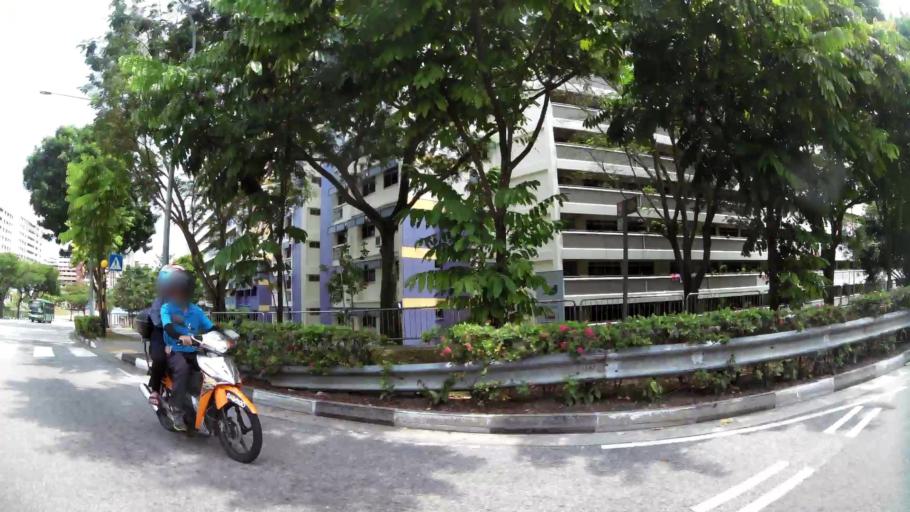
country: MY
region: Johor
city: Johor Bahru
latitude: 1.3397
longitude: 103.6951
